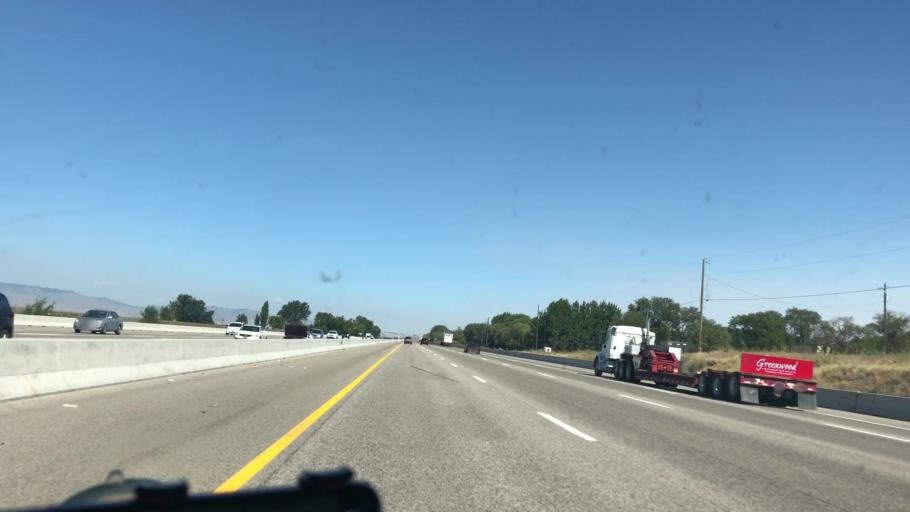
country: US
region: Idaho
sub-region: Ada County
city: Meridian
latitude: 43.5979
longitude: -116.4810
